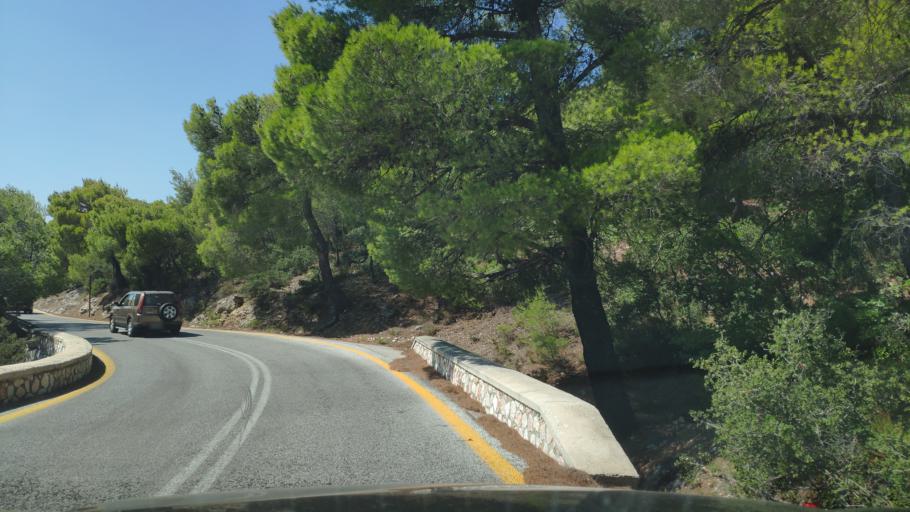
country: GR
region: Attica
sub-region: Nomarchia Anatolikis Attikis
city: Thrakomakedones
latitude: 38.1385
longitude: 23.7309
